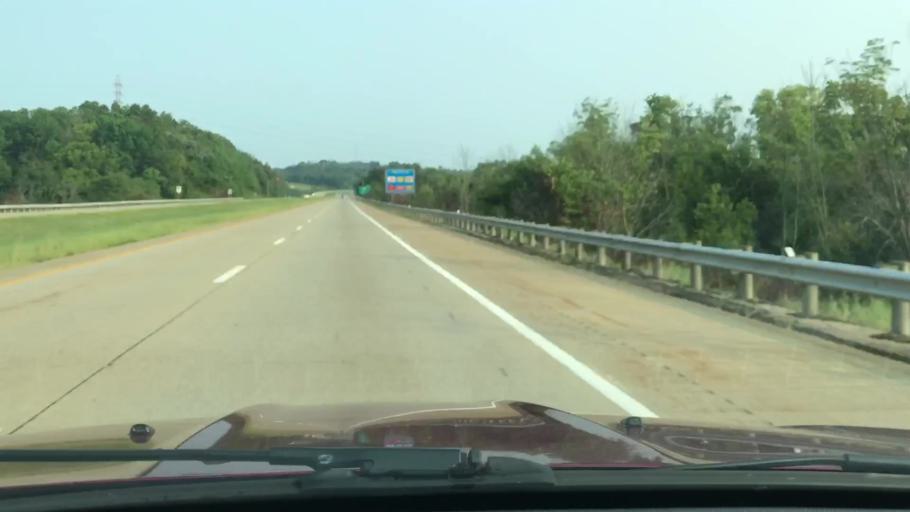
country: US
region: Ohio
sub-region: Noble County
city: Caldwell
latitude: 39.7306
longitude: -81.5245
